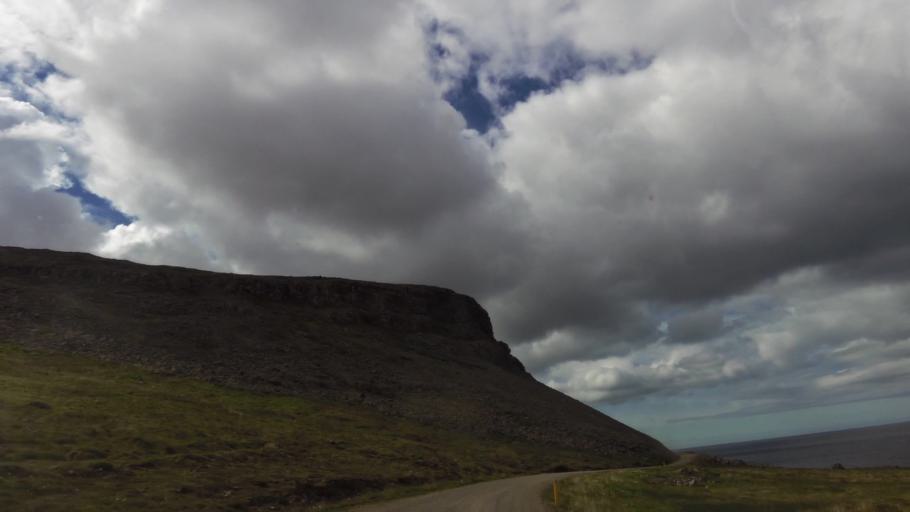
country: IS
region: West
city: Olafsvik
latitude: 65.5615
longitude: -24.0339
